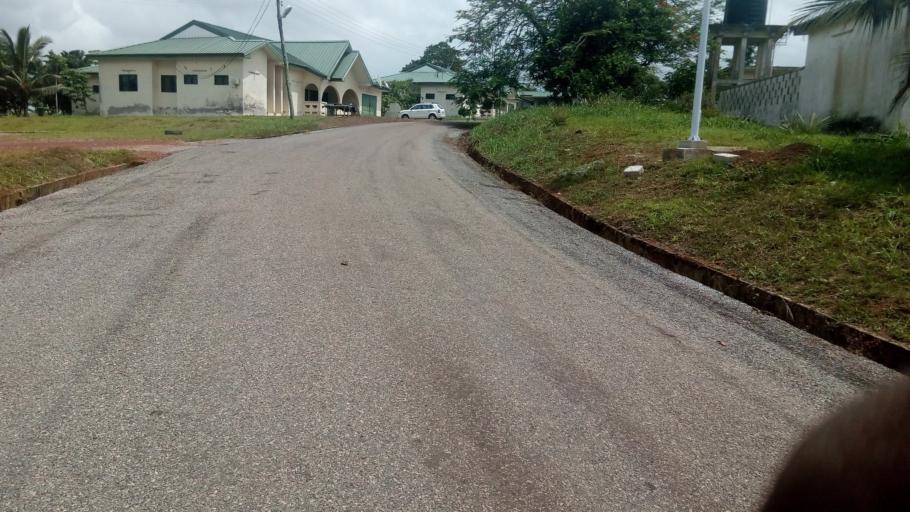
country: GH
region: Western
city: Tarkwa
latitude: 5.2957
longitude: -2.0128
